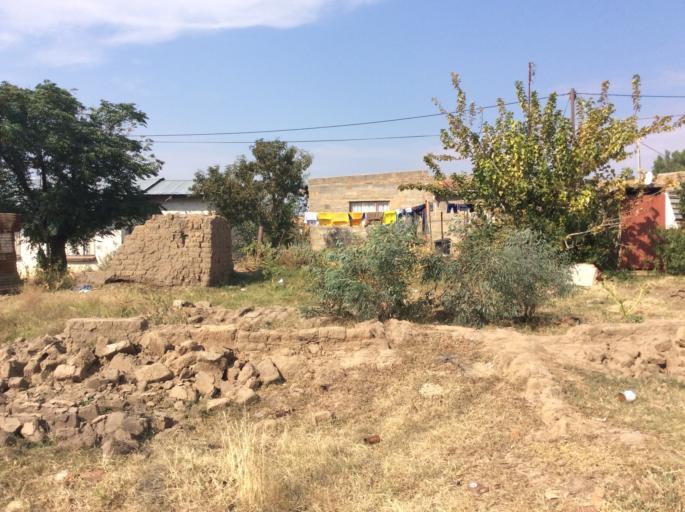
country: ZA
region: Orange Free State
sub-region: Xhariep District Municipality
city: Dewetsdorp
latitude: -29.5883
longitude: 26.6750
